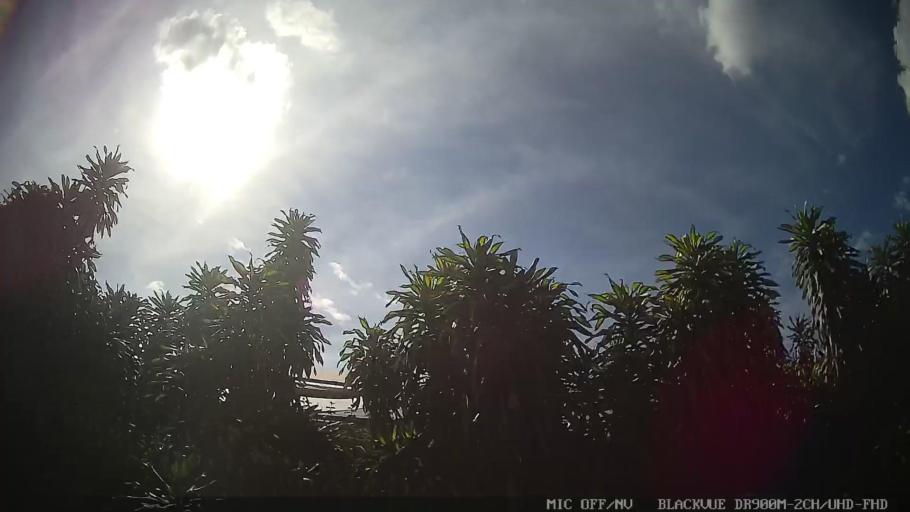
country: BR
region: Sao Paulo
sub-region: Cosmopolis
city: Cosmopolis
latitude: -22.6464
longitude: -47.0949
